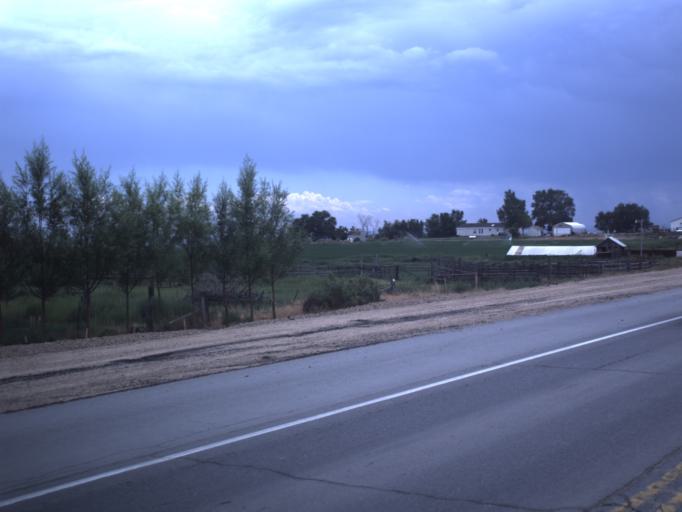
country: US
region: Utah
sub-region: Duchesne County
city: Roosevelt
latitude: 40.2360
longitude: -110.0675
